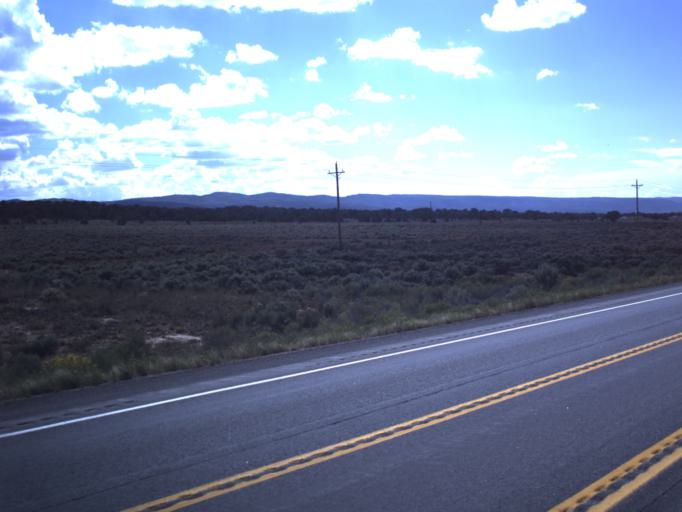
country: US
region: Utah
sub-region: Duchesne County
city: Duchesne
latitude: 40.2034
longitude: -110.7162
